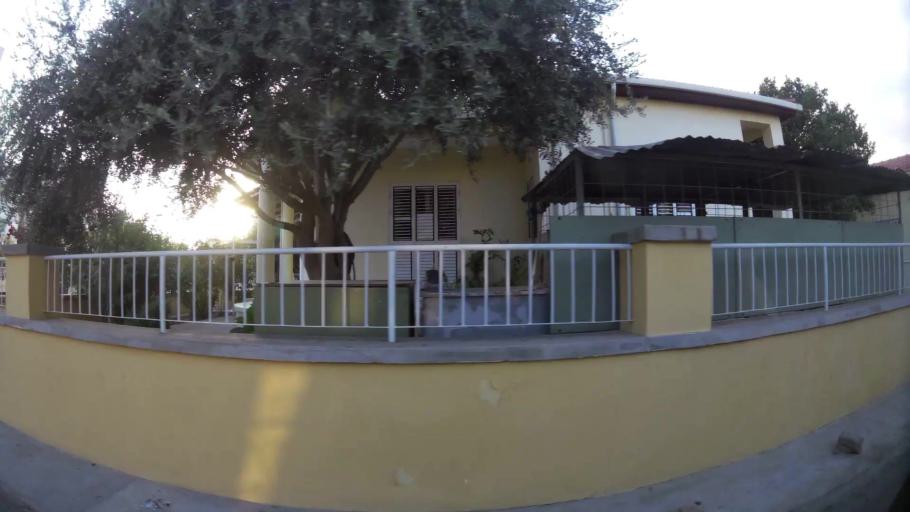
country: CY
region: Lefkosia
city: Nicosia
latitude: 35.1898
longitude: 33.3698
